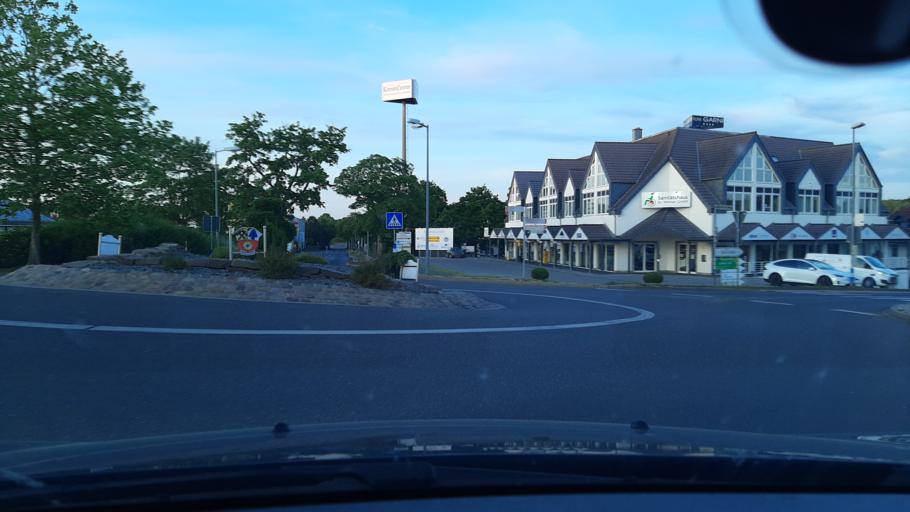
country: DE
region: North Rhine-Westphalia
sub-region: Regierungsbezirk Koln
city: Mechernich
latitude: 50.6170
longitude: 6.6557
